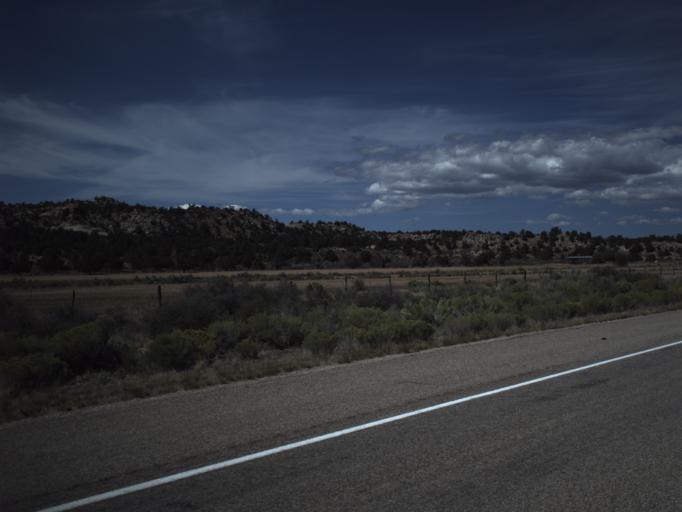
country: US
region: Utah
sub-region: Washington County
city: Ivins
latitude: 37.2573
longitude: -113.6332
